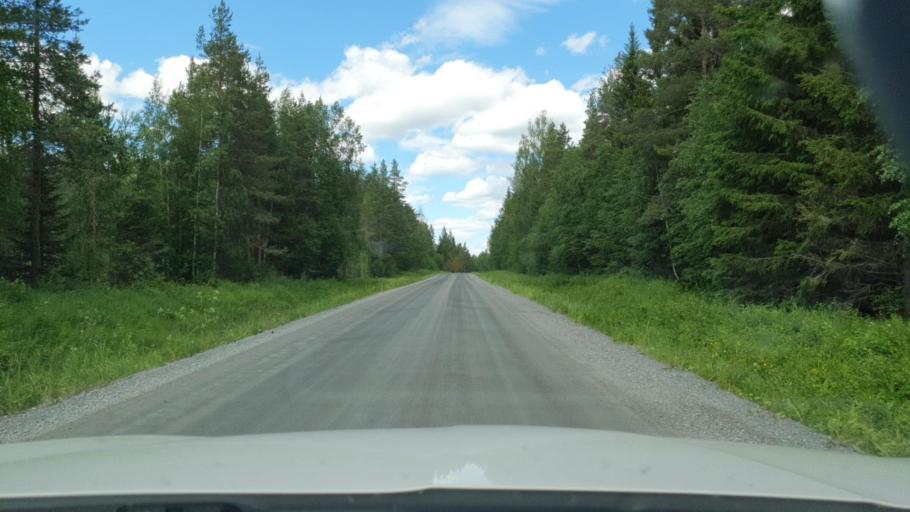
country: SE
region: Vaesterbotten
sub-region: Skelleftea Kommun
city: Forsbacka
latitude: 64.8242
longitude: 20.4970
